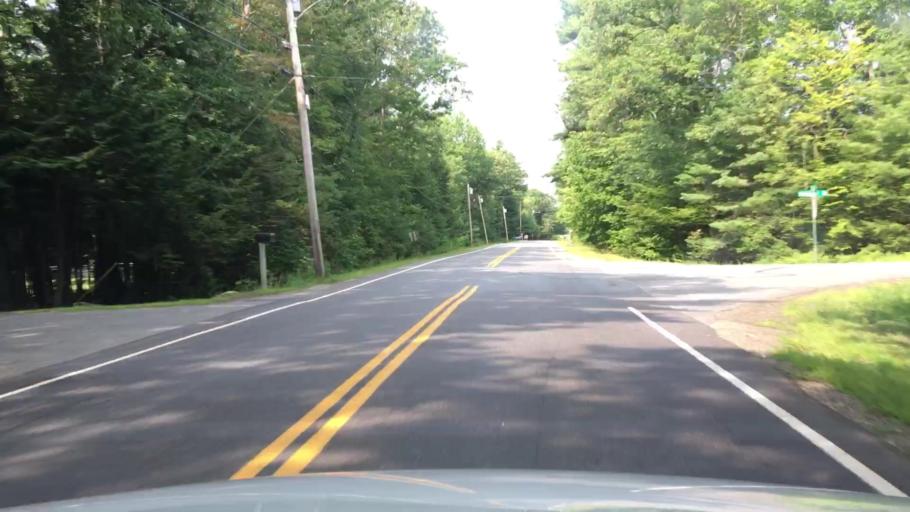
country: US
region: Maine
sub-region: Kennebec County
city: Chelsea
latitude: 44.3130
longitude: -69.6967
